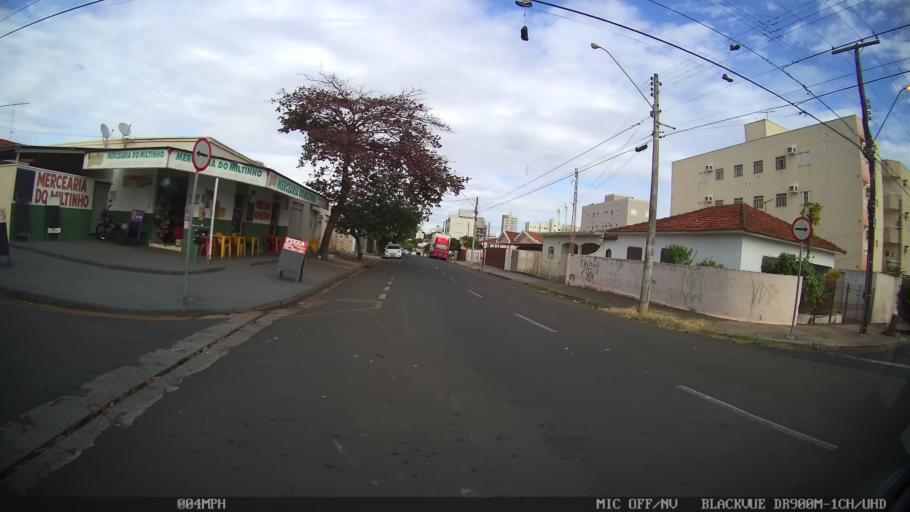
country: BR
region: Sao Paulo
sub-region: Sao Jose Do Rio Preto
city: Sao Jose do Rio Preto
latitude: -20.8318
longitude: -49.3797
